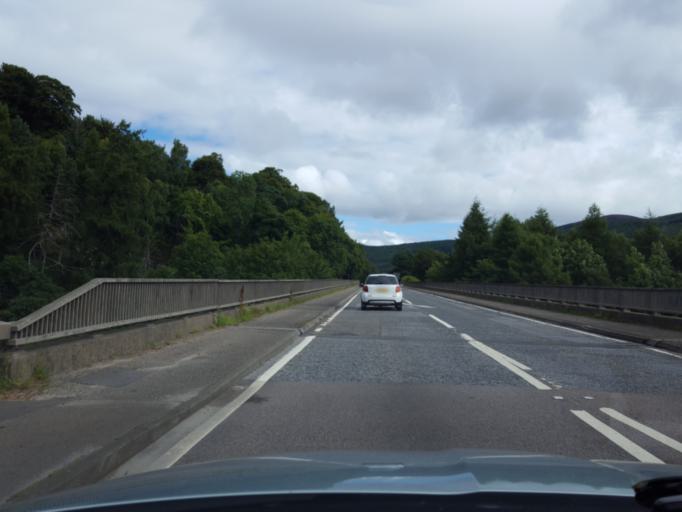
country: GB
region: Scotland
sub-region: Moray
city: Rothes
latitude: 57.4907
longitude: -3.1921
